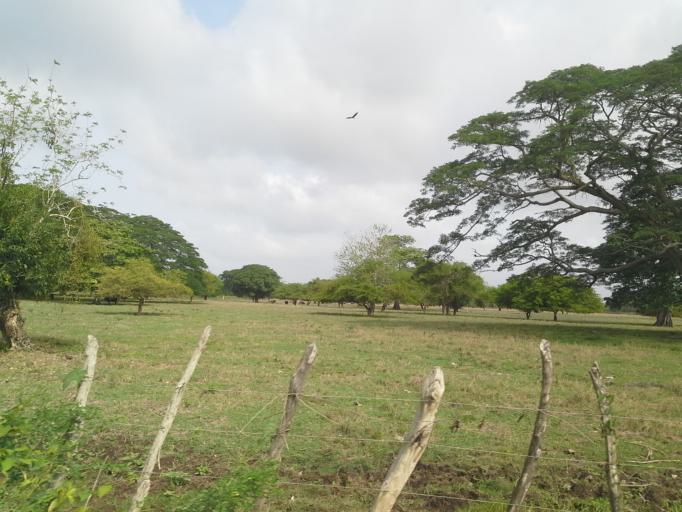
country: CO
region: Cordoba
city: Chima
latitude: 9.1762
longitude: -75.6142
